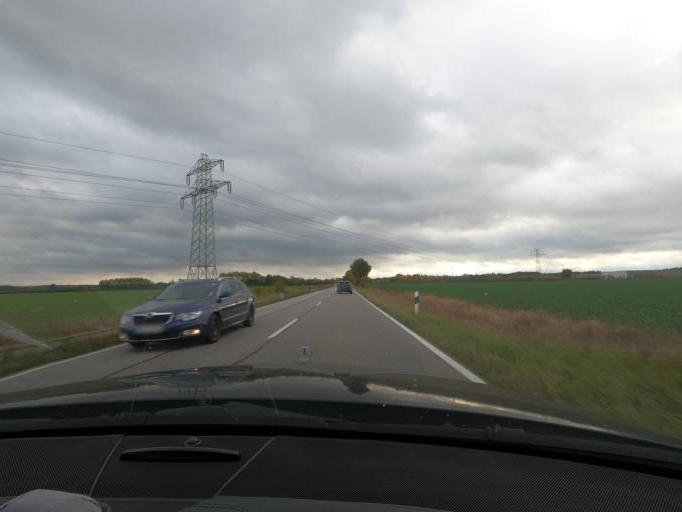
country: DE
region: Schleswig-Holstein
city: Hohenhorn
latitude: 53.4622
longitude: 10.3686
